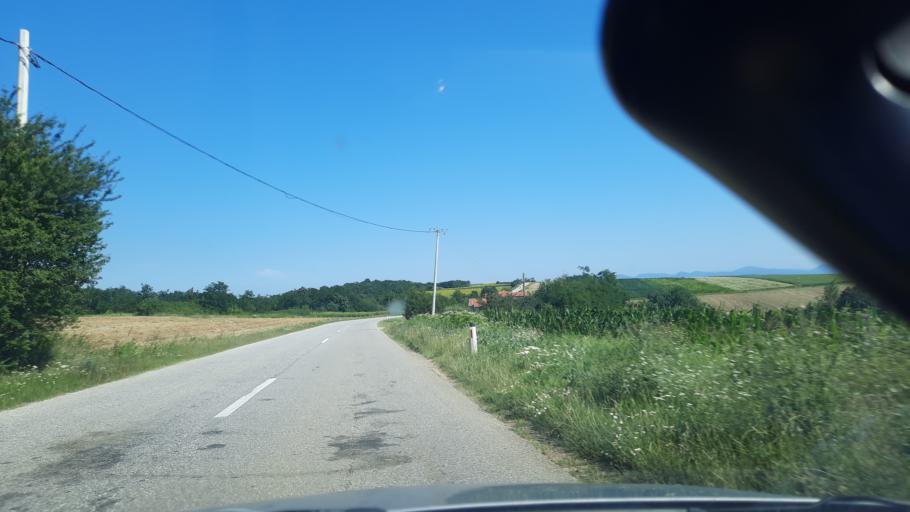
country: RS
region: Central Serbia
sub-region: Branicevski Okrug
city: Malo Crnice
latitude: 44.5825
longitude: 21.4147
